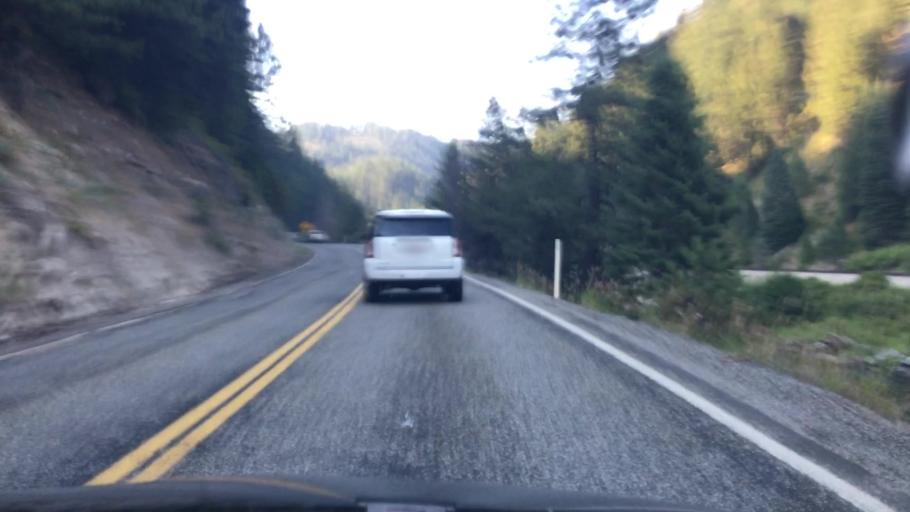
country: US
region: Idaho
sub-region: Valley County
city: Cascade
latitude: 44.3224
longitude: -116.0604
